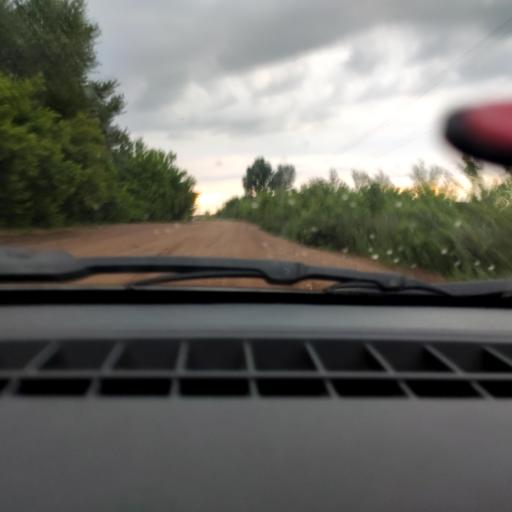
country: RU
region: Bashkortostan
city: Blagoveshchensk
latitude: 54.9160
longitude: 55.9864
